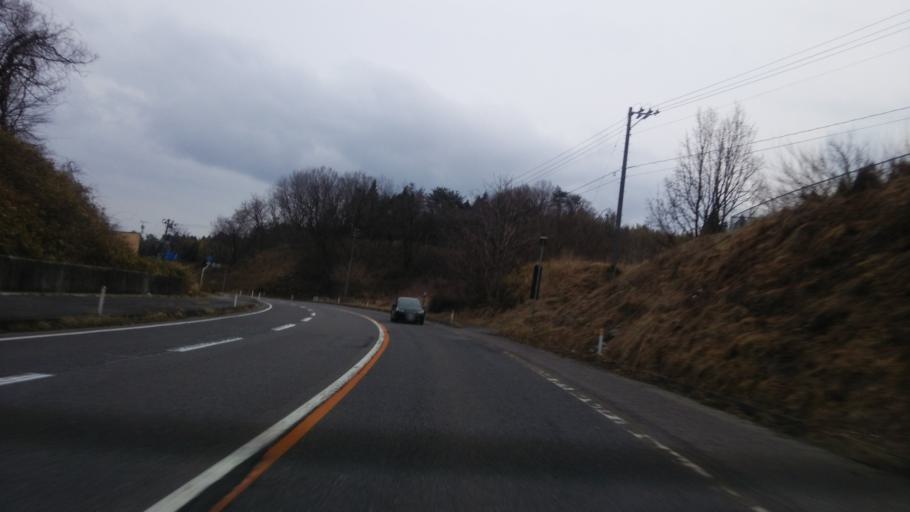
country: JP
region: Fukushima
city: Ishikawa
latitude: 37.2725
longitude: 140.5493
